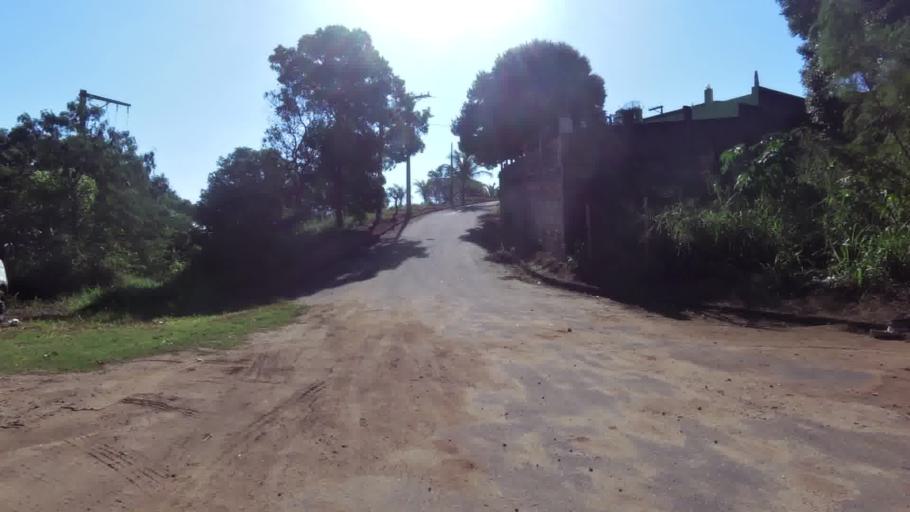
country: BR
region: Espirito Santo
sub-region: Guarapari
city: Guarapari
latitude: -20.7468
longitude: -40.5595
